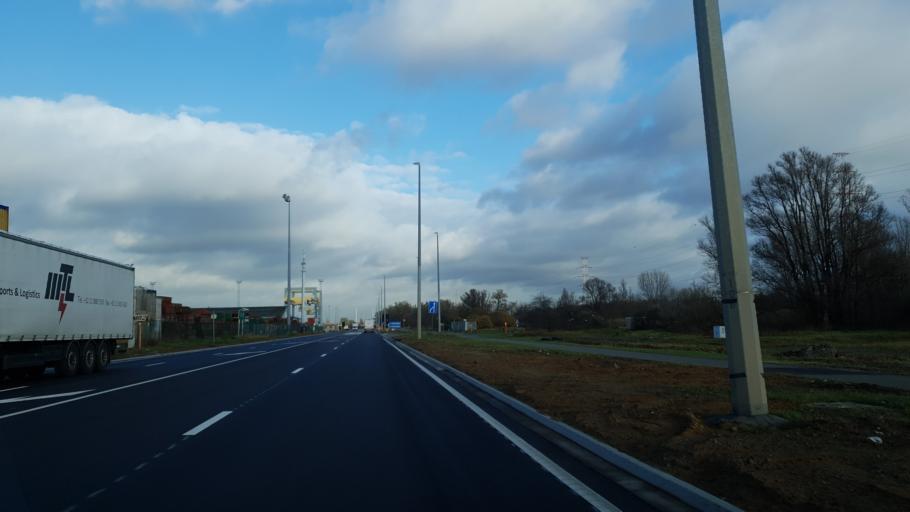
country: BE
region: Flanders
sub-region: Provincie Antwerpen
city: Stabroek
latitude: 51.2800
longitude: 4.3851
